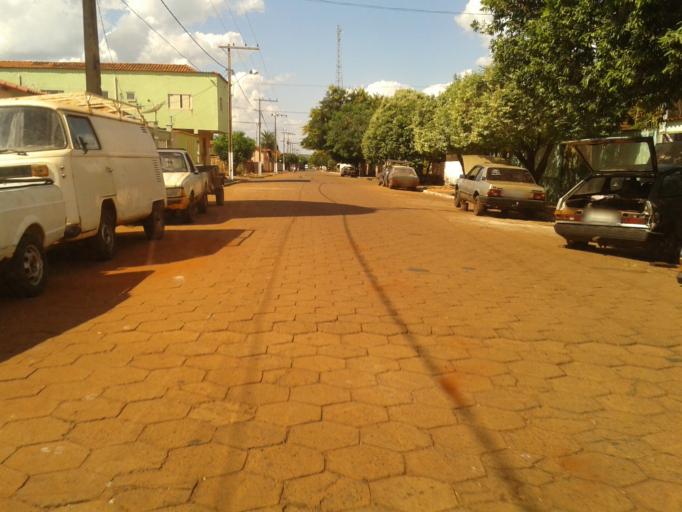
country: BR
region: Minas Gerais
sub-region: Santa Vitoria
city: Santa Vitoria
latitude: -18.6934
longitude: -49.9483
